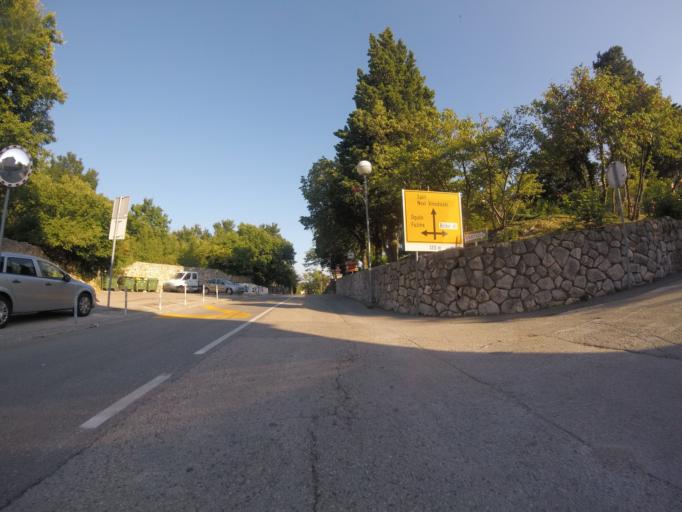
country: HR
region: Primorsko-Goranska
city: Bribir
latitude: 45.1629
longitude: 14.7598
